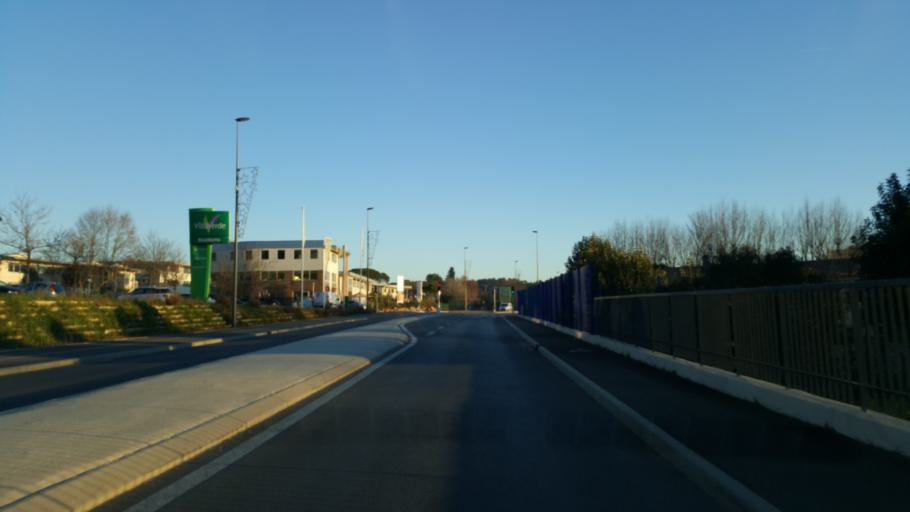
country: FR
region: Provence-Alpes-Cote d'Azur
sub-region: Departement des Bouches-du-Rhone
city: Meyreuil
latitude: 43.4965
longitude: 5.5208
